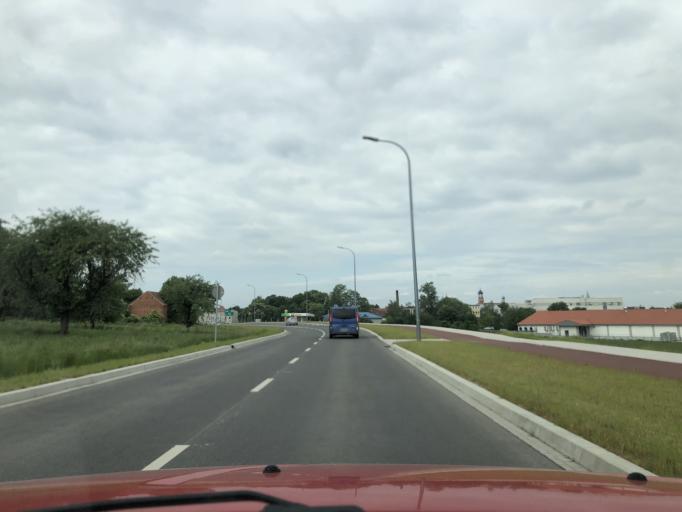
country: PL
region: Greater Poland Voivodeship
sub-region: Powiat jarocinski
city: Jarocin
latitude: 51.9683
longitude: 17.5101
